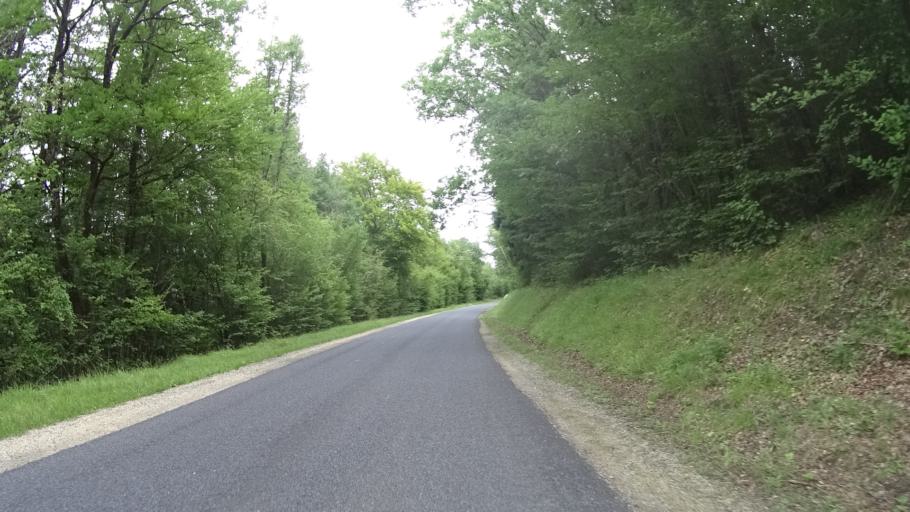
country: FR
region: Lorraine
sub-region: Departement de la Meuse
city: Lerouville
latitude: 48.8034
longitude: 5.5025
